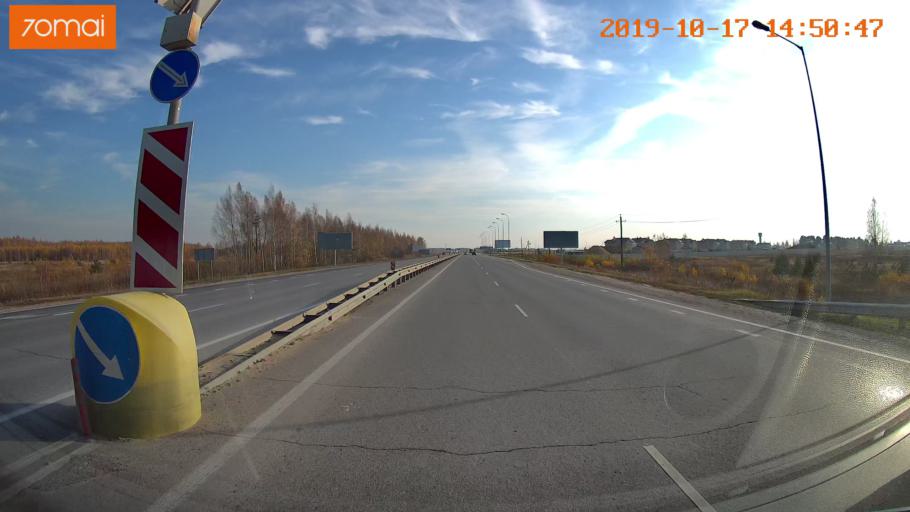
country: RU
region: Rjazan
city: Polyany
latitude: 54.7292
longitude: 39.8445
